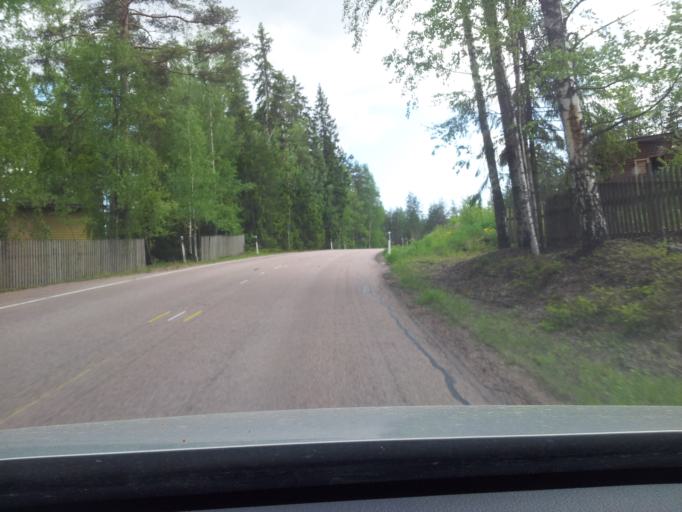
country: FI
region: South Karelia
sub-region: Lappeenranta
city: Luumaeki
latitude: 60.9489
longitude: 27.5832
